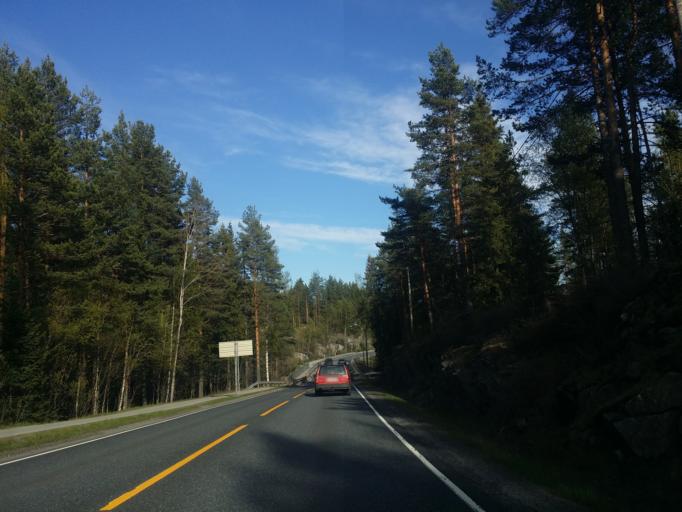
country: NO
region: Buskerud
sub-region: Kongsberg
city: Kongsberg
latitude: 59.6250
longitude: 9.6083
